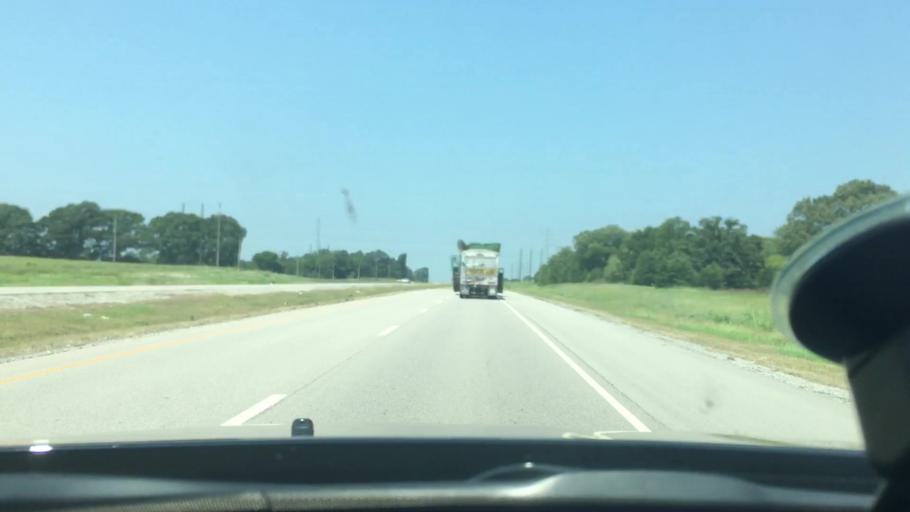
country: US
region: Oklahoma
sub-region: Atoka County
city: Atoka
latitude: 34.3277
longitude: -96.0456
